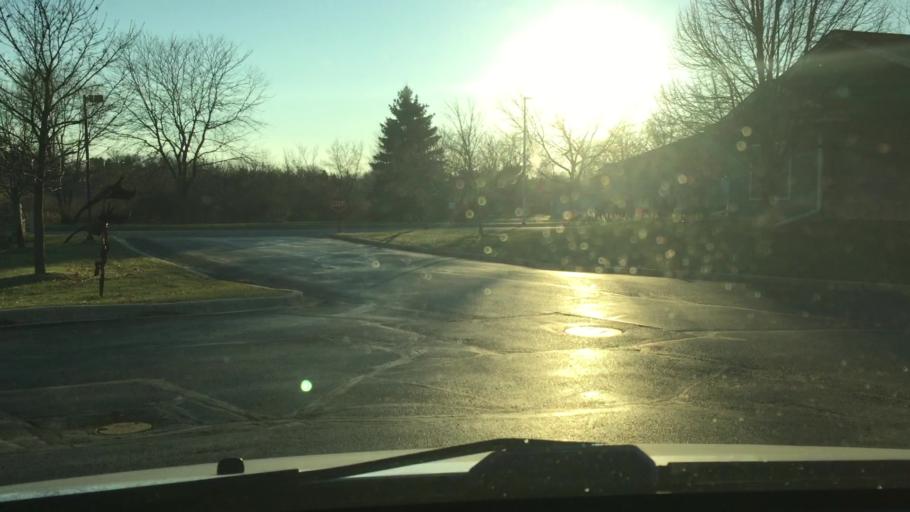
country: US
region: Wisconsin
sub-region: Waukesha County
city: Pewaukee
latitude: 43.0919
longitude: -88.2772
